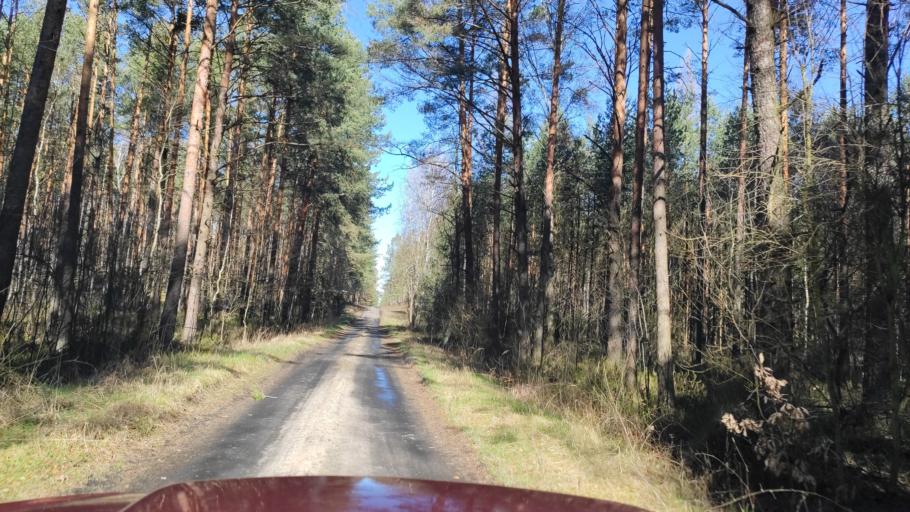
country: PL
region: Masovian Voivodeship
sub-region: Powiat zwolenski
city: Zwolen
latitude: 51.4109
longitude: 21.5566
